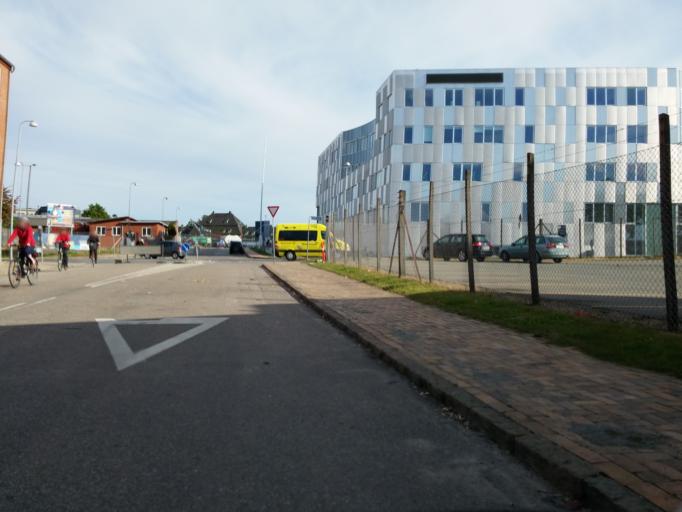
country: DK
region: South Denmark
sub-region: Odense Kommune
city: Odense
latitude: 55.4040
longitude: 10.3833
